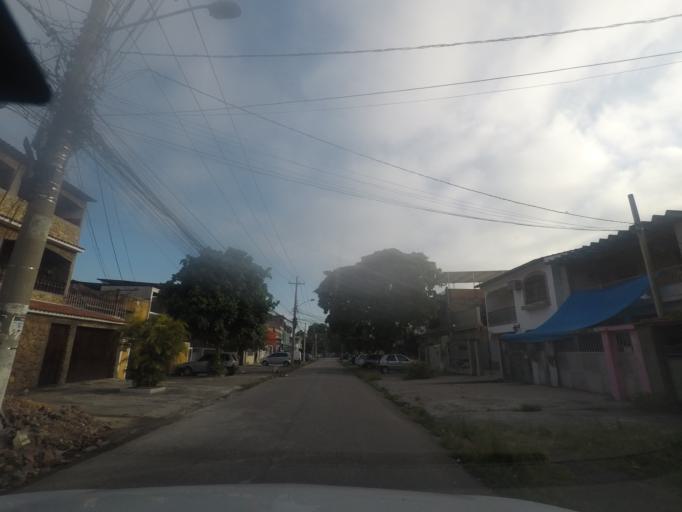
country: BR
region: Rio de Janeiro
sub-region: Duque De Caxias
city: Duque de Caxias
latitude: -22.8371
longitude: -43.2716
